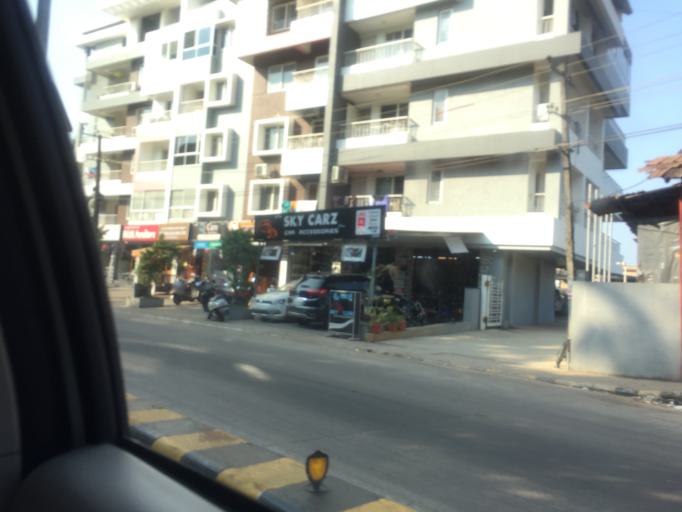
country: IN
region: Karnataka
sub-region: Dakshina Kannada
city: Ullal
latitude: 12.8511
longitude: 74.8446
